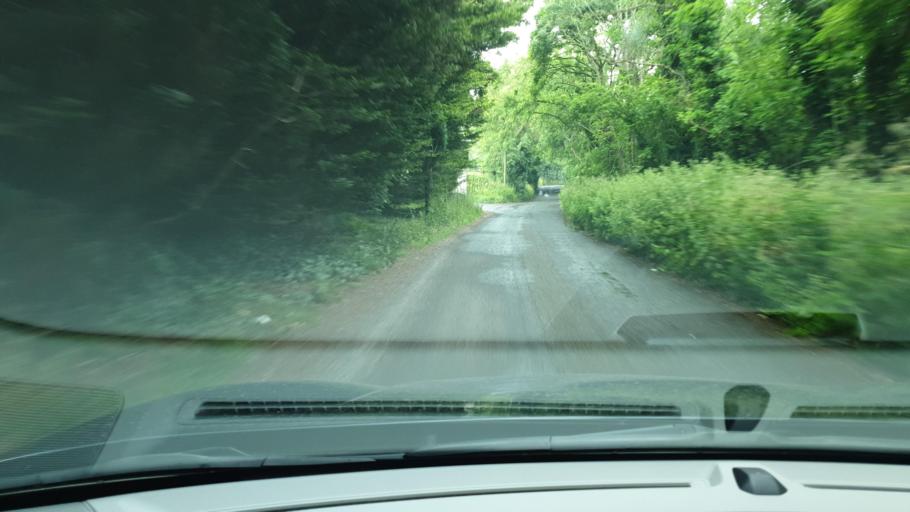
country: IE
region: Leinster
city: Hartstown
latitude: 53.4217
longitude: -6.4079
